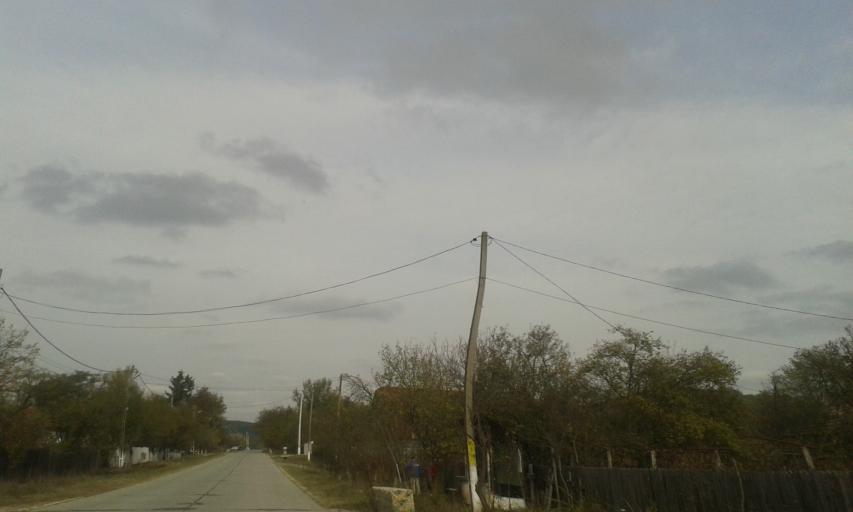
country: RO
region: Gorj
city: Logresti
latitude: 44.8695
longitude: 23.7042
